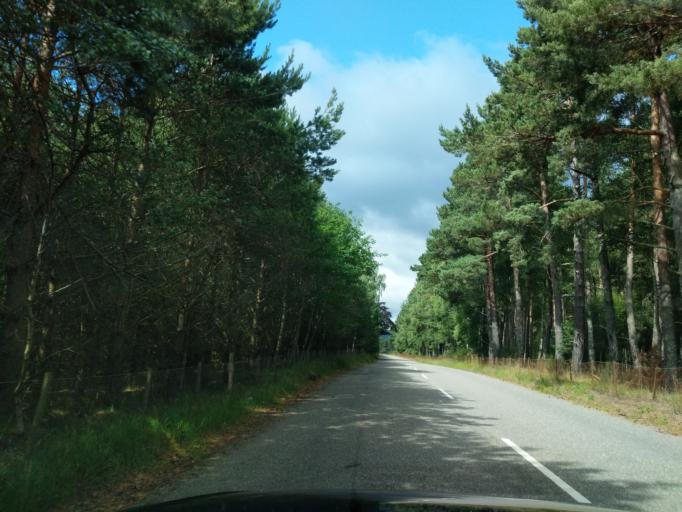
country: GB
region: Scotland
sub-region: Aberdeenshire
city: Aboyne
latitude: 57.0707
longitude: -2.8611
